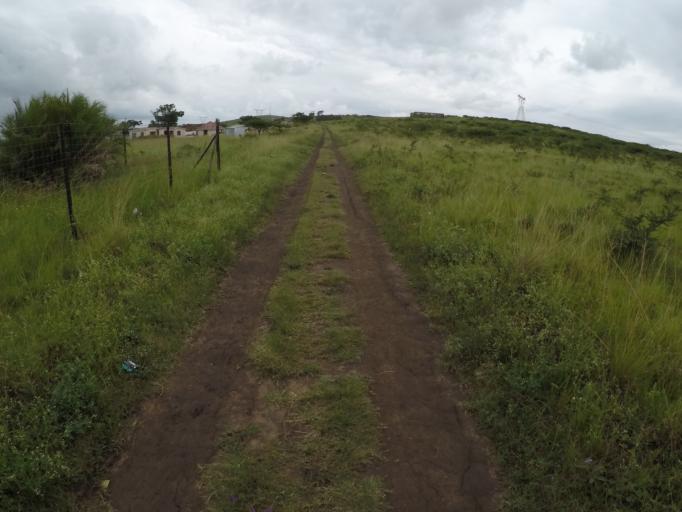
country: ZA
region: KwaZulu-Natal
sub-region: uThungulu District Municipality
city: Empangeni
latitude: -28.7113
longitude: 31.8573
